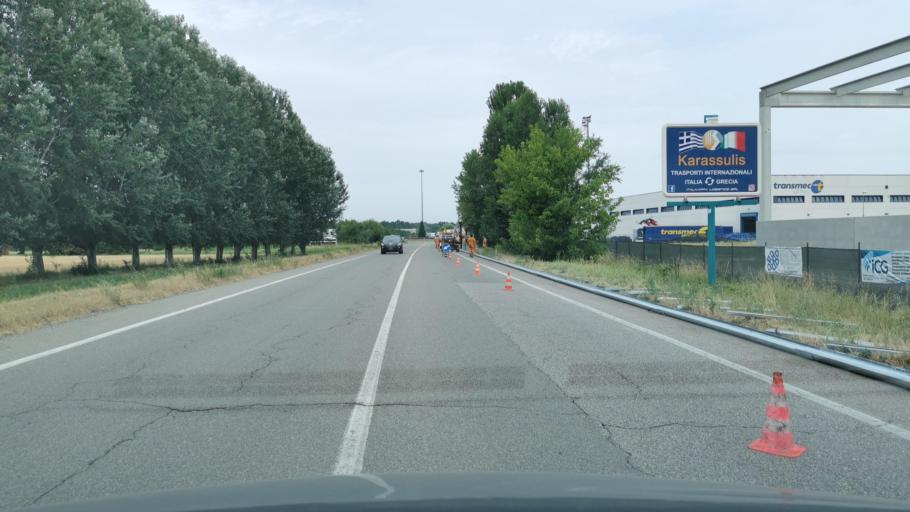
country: IT
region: Emilia-Romagna
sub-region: Provincia di Modena
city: Campogalliano
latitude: 44.6827
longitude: 10.8615
